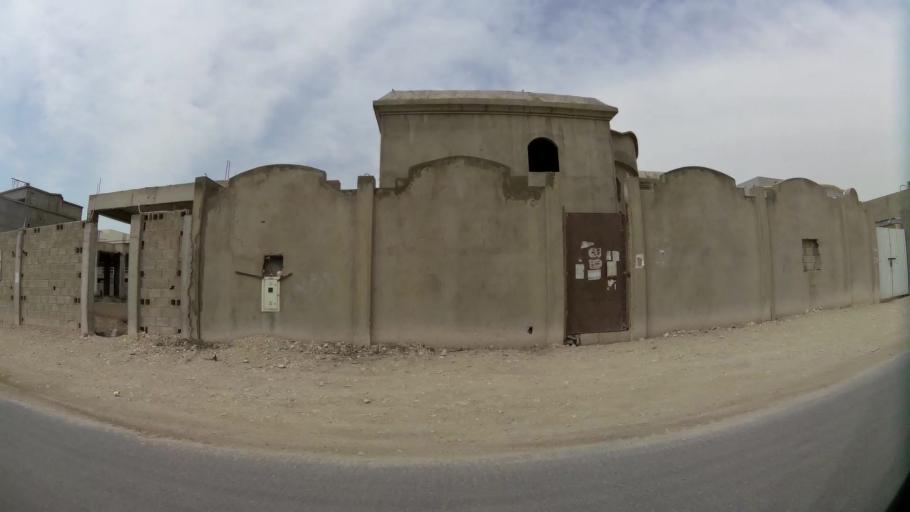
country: QA
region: Al Wakrah
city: Al Wukayr
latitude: 25.1969
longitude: 51.4545
